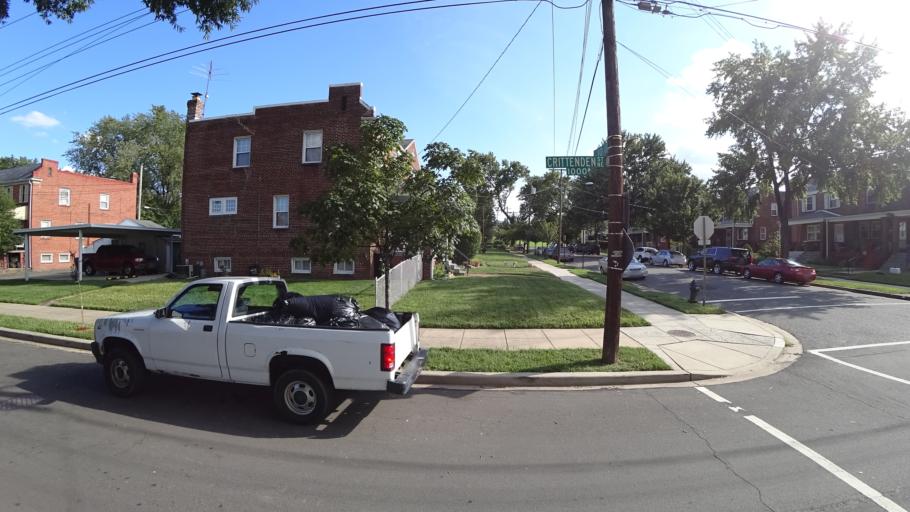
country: US
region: Maryland
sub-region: Prince George's County
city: Chillum
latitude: 38.9473
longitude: -76.9925
